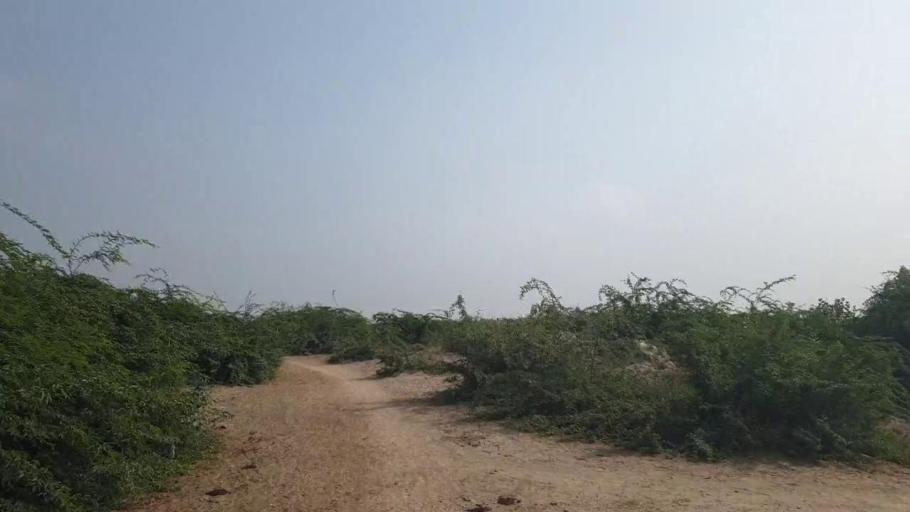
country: PK
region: Sindh
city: Badin
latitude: 24.5476
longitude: 68.7034
